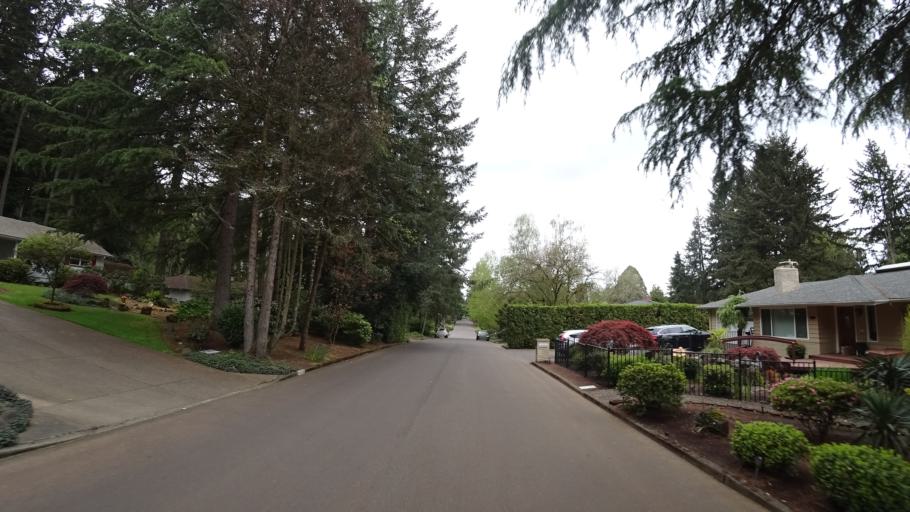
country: US
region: Oregon
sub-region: Washington County
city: Beaverton
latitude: 45.4628
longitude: -122.8212
